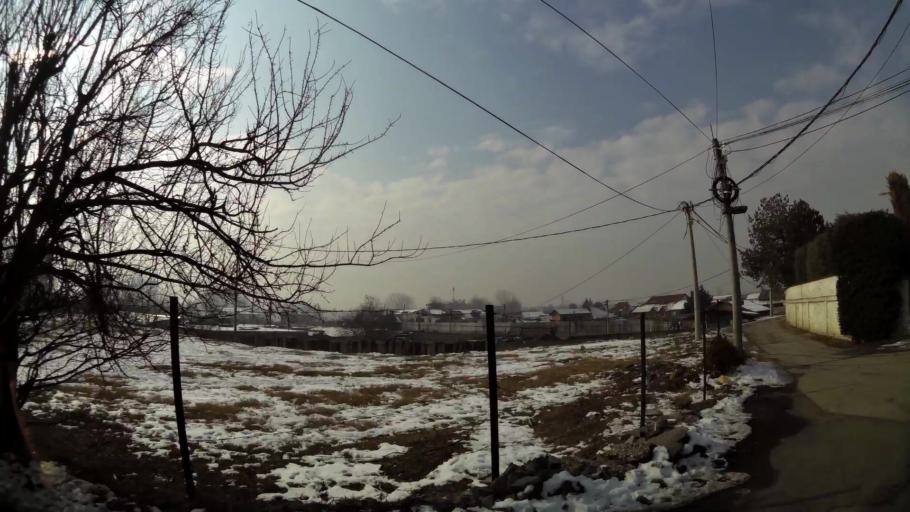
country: MK
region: Suto Orizari
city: Suto Orizare
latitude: 42.0156
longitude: 21.3873
